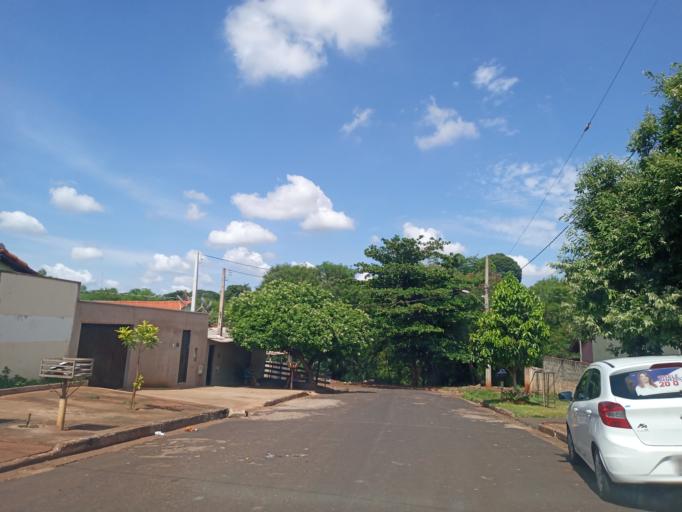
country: BR
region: Minas Gerais
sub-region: Ituiutaba
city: Ituiutaba
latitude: -18.9873
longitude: -49.4741
